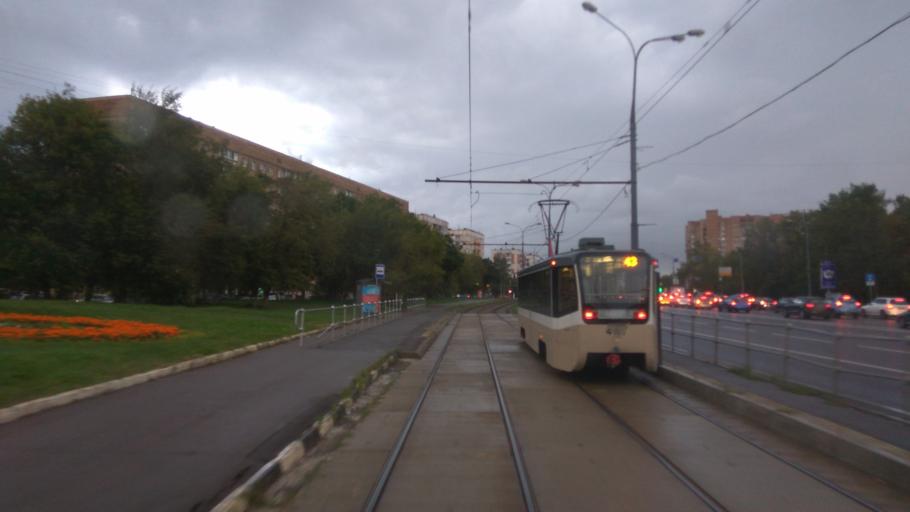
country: RU
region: Moscow
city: Taganskiy
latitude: 55.7271
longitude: 37.6633
